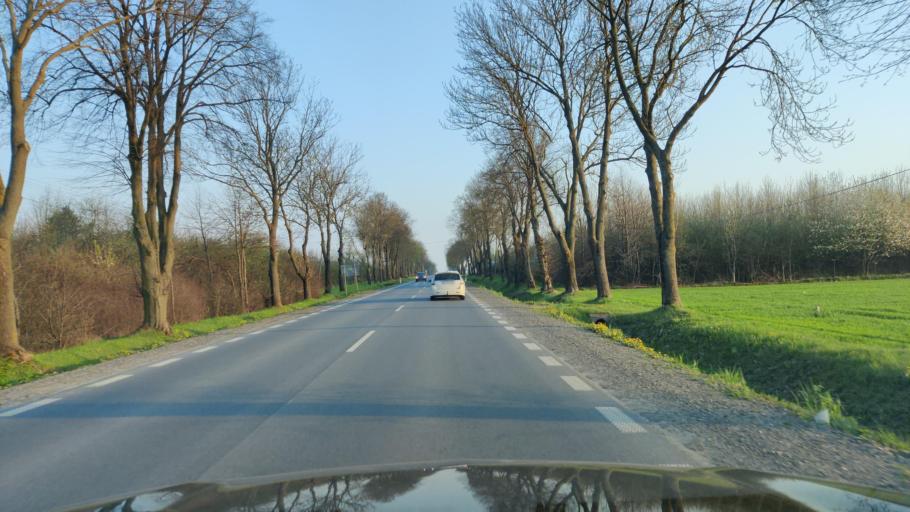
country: PL
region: Masovian Voivodeship
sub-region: Powiat pultuski
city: Pultusk
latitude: 52.6852
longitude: 21.0807
